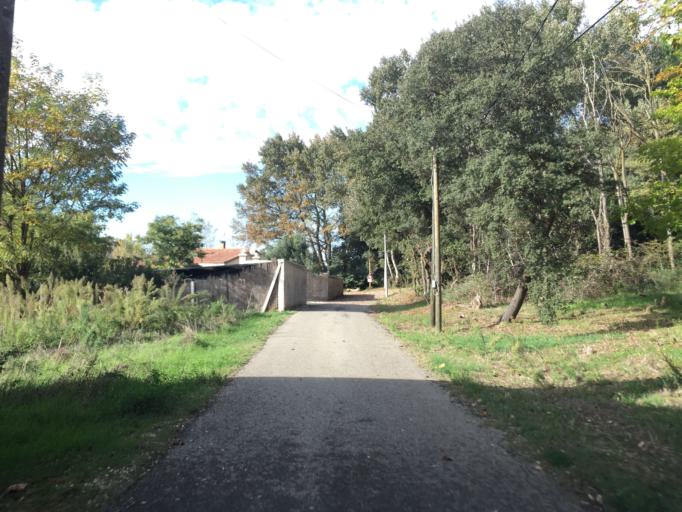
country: FR
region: Provence-Alpes-Cote d'Azur
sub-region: Departement du Vaucluse
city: Orange
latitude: 44.1037
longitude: 4.8076
